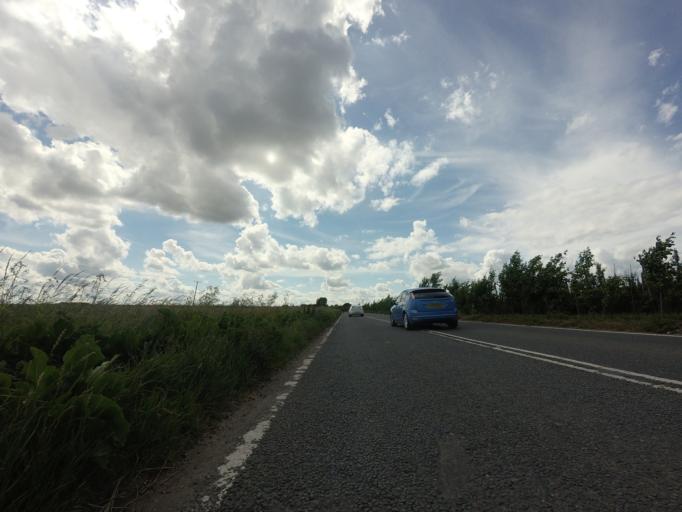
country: GB
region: England
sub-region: Medway
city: Stoke
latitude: 51.4489
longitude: 0.6076
